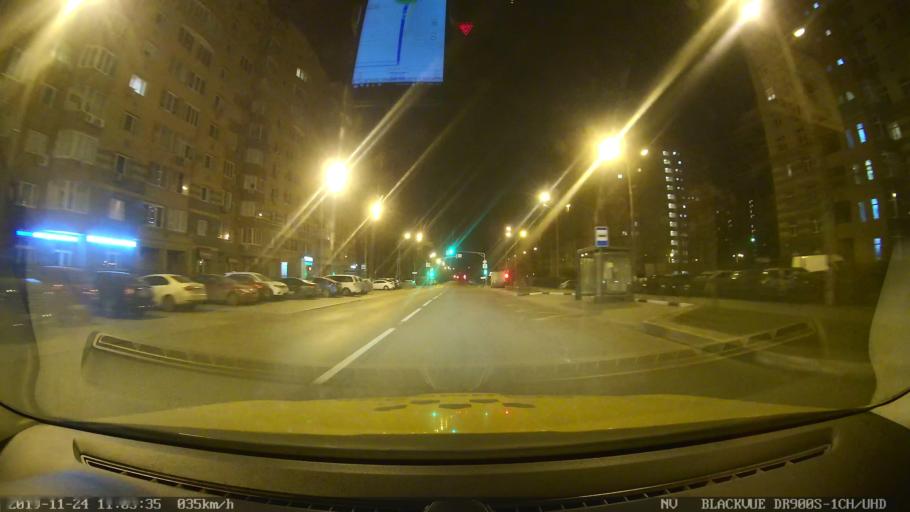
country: RU
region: Moskovskaya
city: Mytishchi
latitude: 55.9027
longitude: 37.7168
